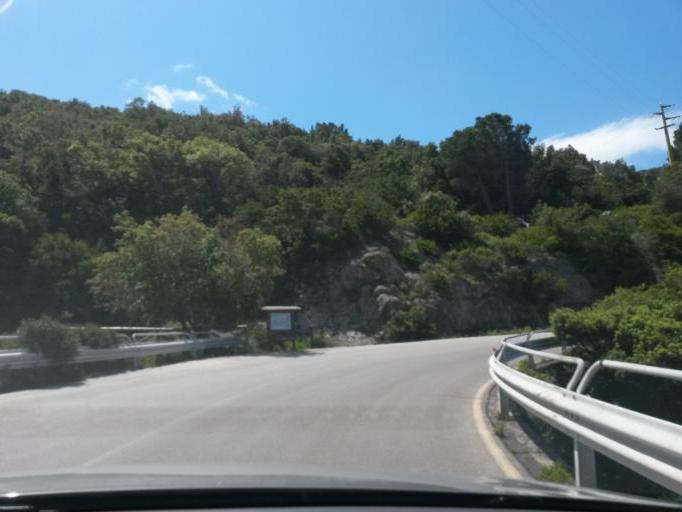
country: IT
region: Tuscany
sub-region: Provincia di Livorno
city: Marciana
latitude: 42.7841
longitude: 10.1122
